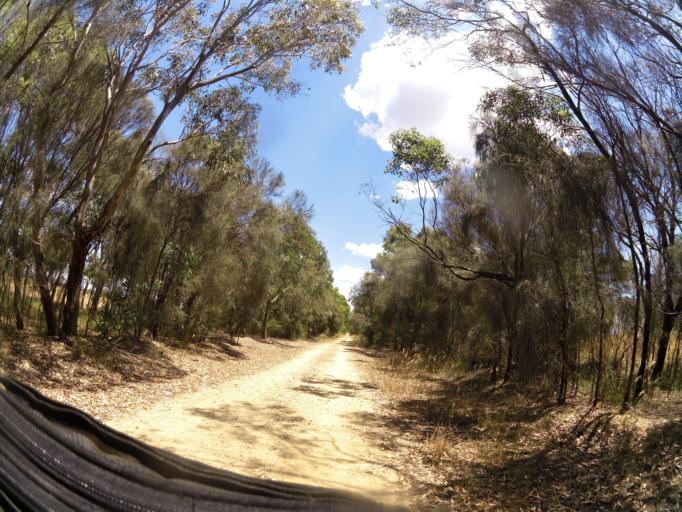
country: AU
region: Victoria
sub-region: Wellington
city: Heyfield
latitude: -37.9811
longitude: 146.8387
